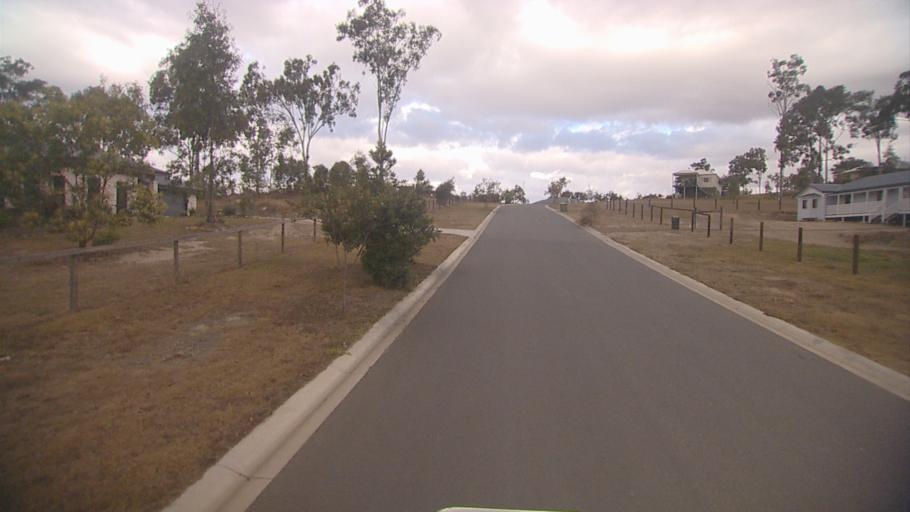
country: AU
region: Queensland
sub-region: Logan
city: Cedar Vale
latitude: -27.8614
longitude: 153.0784
